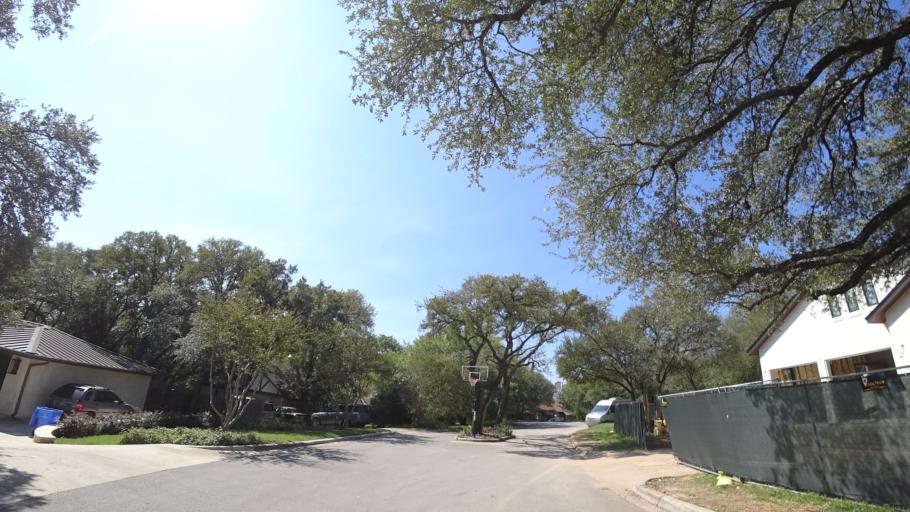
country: US
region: Texas
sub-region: Travis County
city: Rollingwood
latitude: 30.2703
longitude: -97.7842
